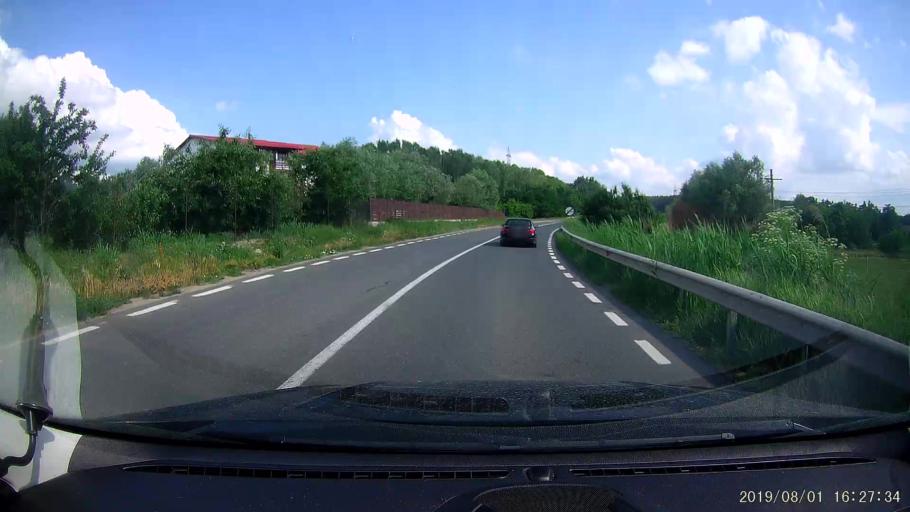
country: RO
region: Calarasi
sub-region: Municipiul Calarasi
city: Calarasi
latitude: 44.1622
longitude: 27.3152
